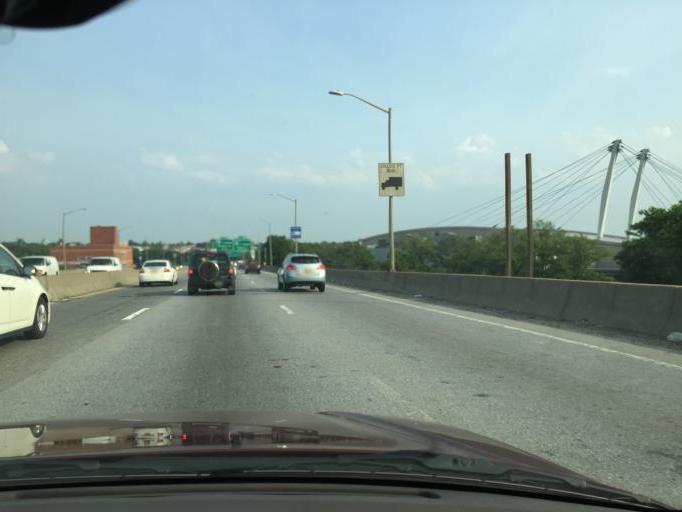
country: US
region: New York
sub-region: Queens County
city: Jamaica
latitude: 40.7532
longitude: -73.8373
